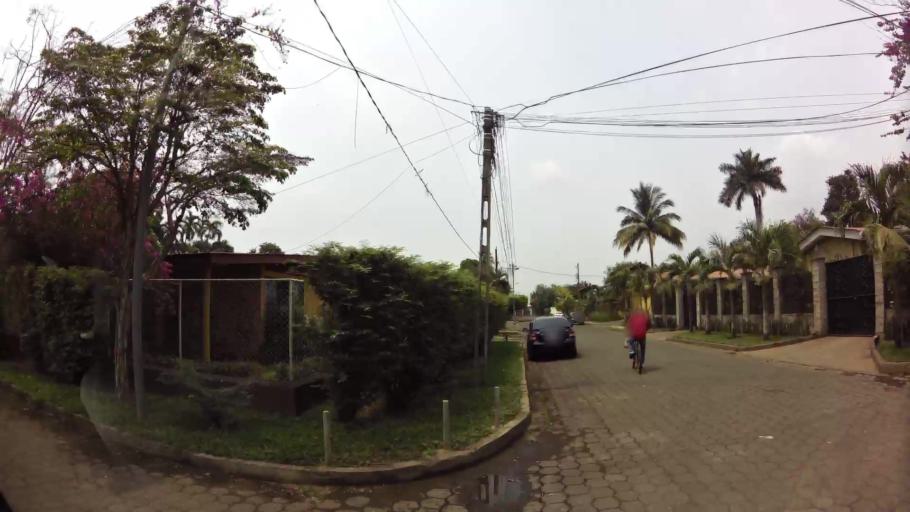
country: NI
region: Chinandega
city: Chinandega
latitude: 12.6311
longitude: -87.1150
